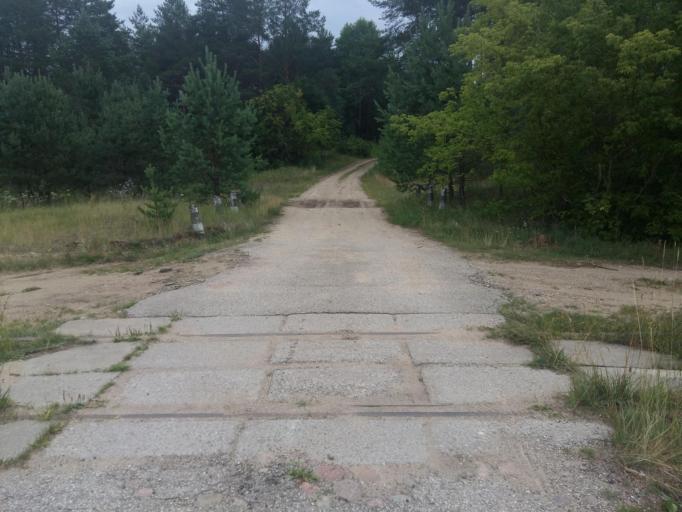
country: LT
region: Alytaus apskritis
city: Druskininkai
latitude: 53.9913
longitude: 24.2938
